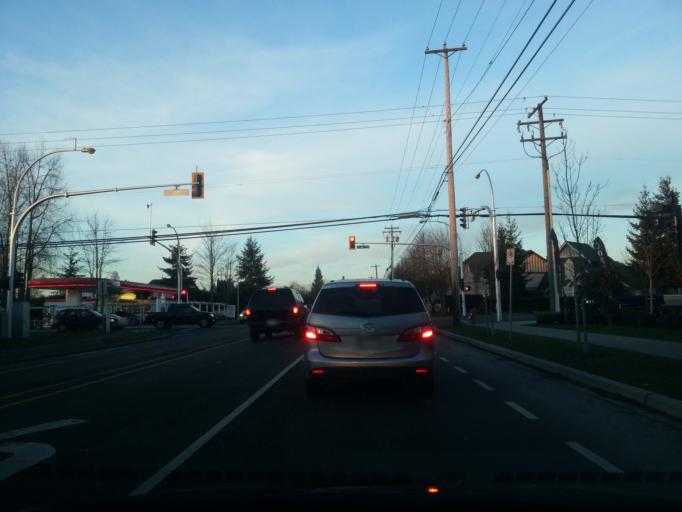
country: CA
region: British Columbia
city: Langley
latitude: 49.1184
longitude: -122.7125
